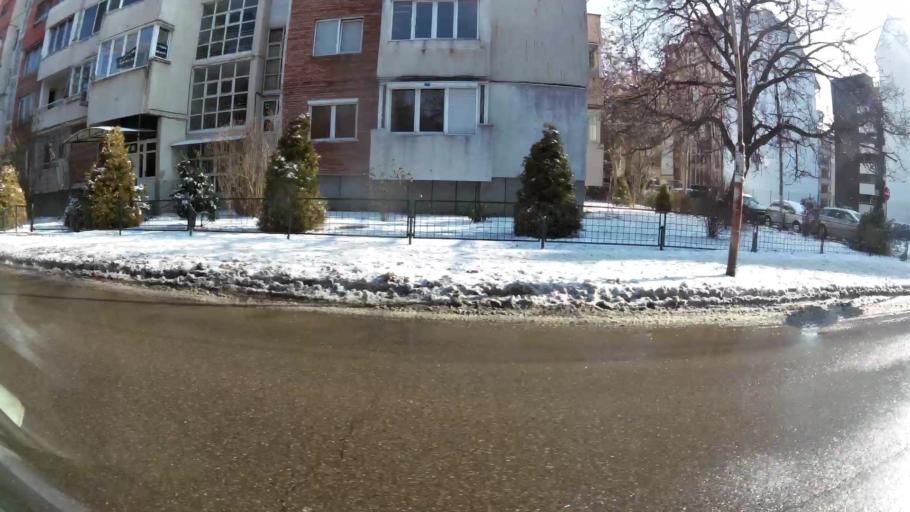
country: BG
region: Sofia-Capital
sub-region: Stolichna Obshtina
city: Sofia
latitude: 42.6620
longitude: 23.3136
